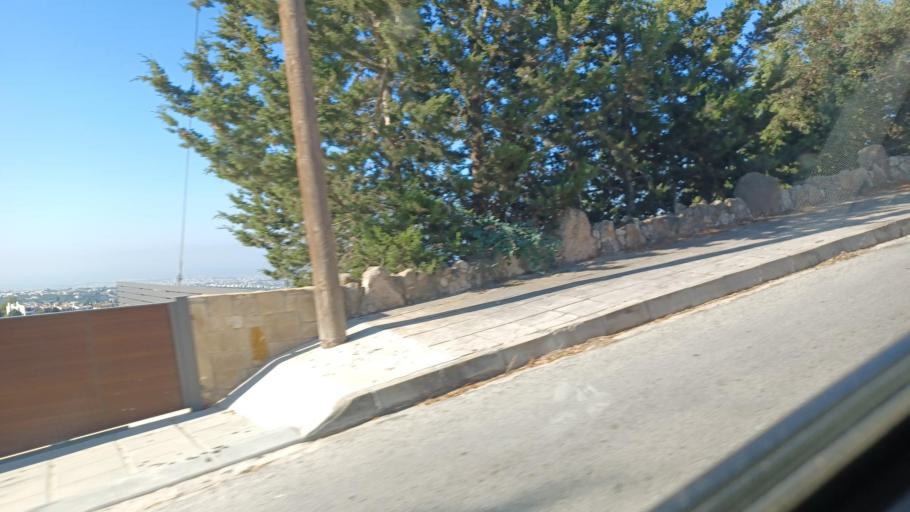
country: CY
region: Pafos
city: Tala
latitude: 34.8439
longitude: 32.4391
